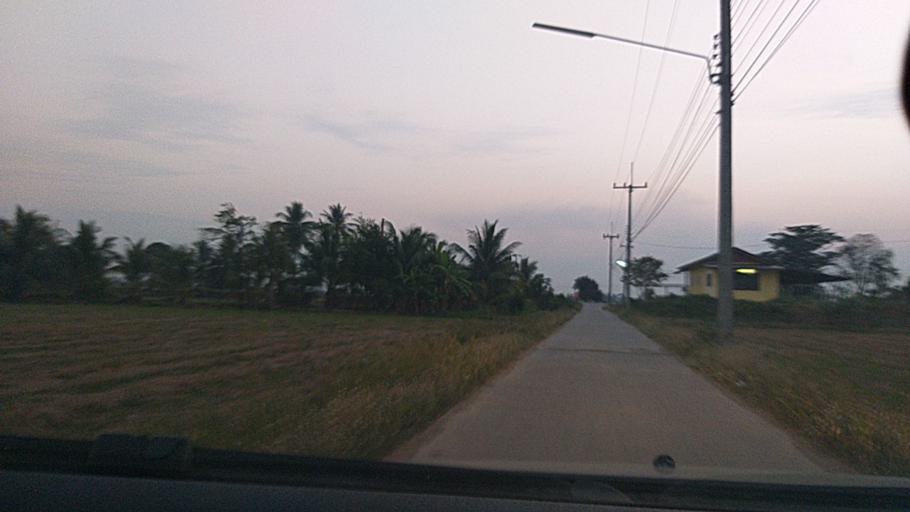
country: TH
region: Sing Buri
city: Sing Buri
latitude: 14.8344
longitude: 100.4003
